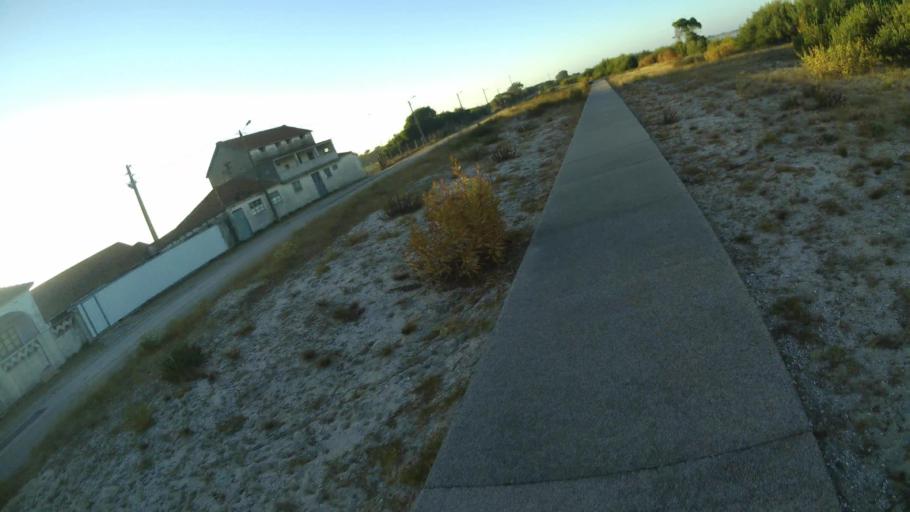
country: PT
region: Aveiro
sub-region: Ilhavo
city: Gafanha da Encarnacao
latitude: 40.5711
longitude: -8.7563
